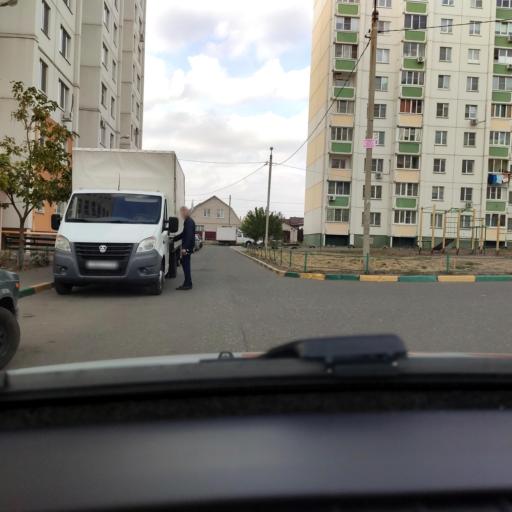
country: RU
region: Voronezj
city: Shilovo
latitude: 51.5617
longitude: 39.1119
